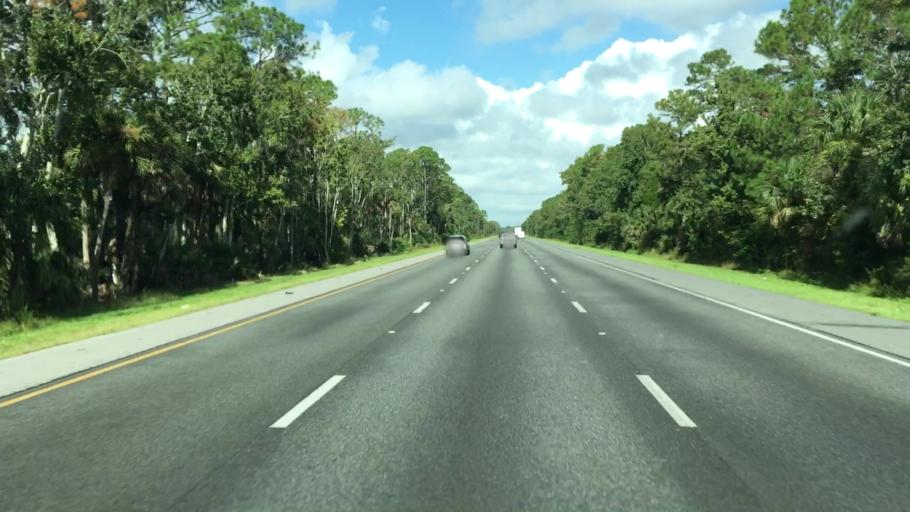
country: US
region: Florida
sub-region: Volusia County
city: Glencoe
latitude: 29.0483
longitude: -81.0068
